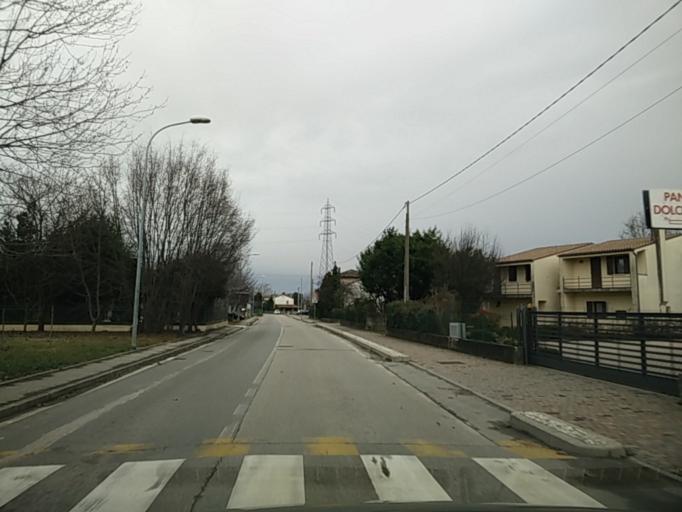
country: IT
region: Veneto
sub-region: Provincia di Treviso
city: Caselle
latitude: 45.7461
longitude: 12.0021
